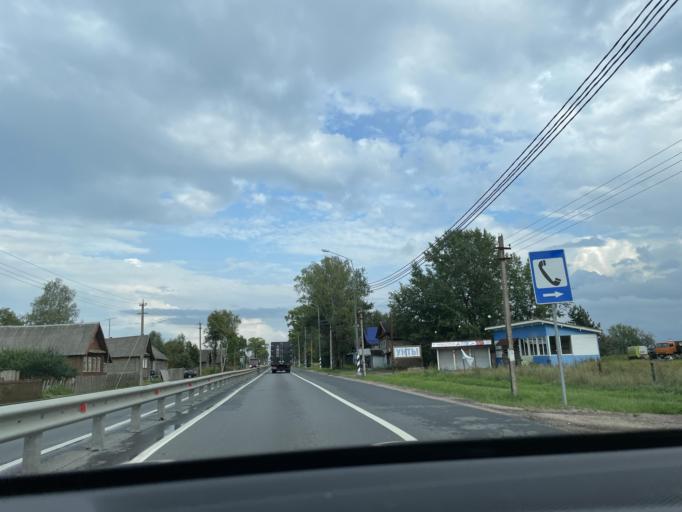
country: RU
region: Tverskaya
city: Kuzhenkino
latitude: 57.7267
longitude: 34.0682
